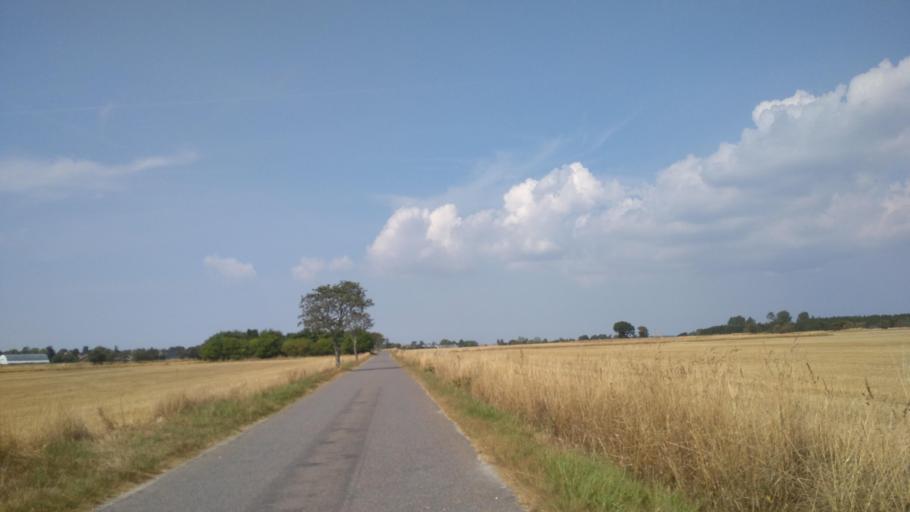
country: DK
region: Capital Region
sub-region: Bornholm Kommune
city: Akirkeby
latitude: 55.0636
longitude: 14.9377
